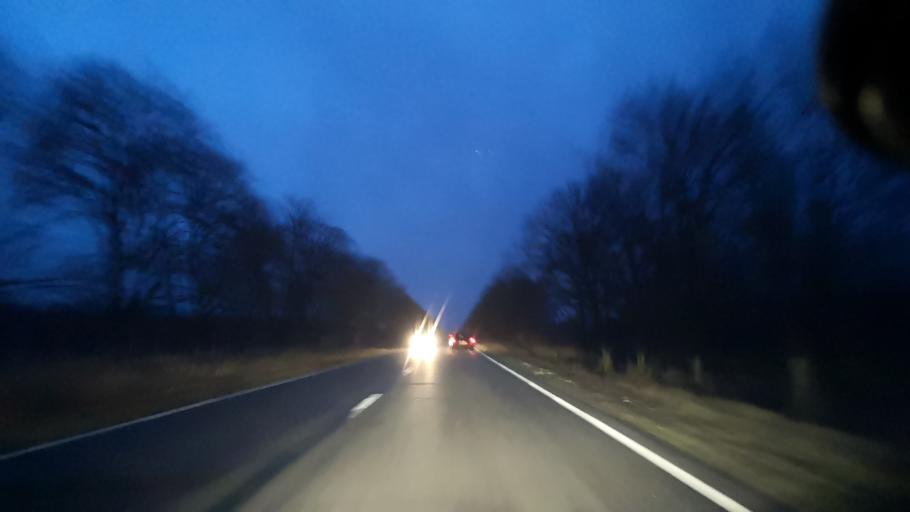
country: MD
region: Orhei
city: Orhei
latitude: 47.4677
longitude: 28.7914
